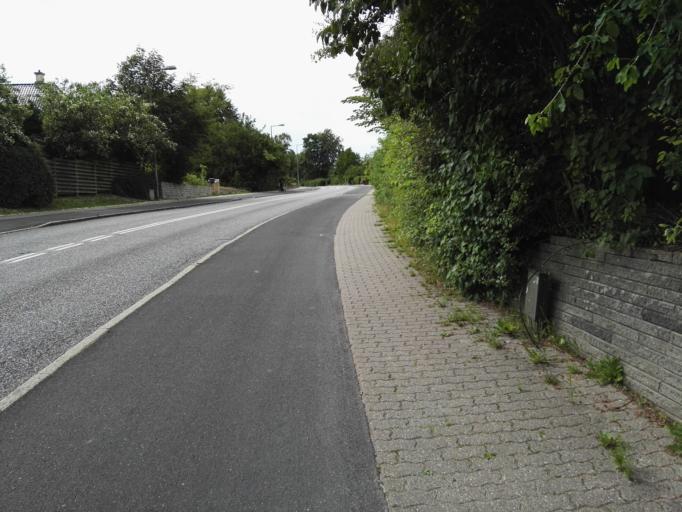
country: DK
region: Capital Region
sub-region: Ballerup Kommune
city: Malov
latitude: 55.7521
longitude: 12.3134
